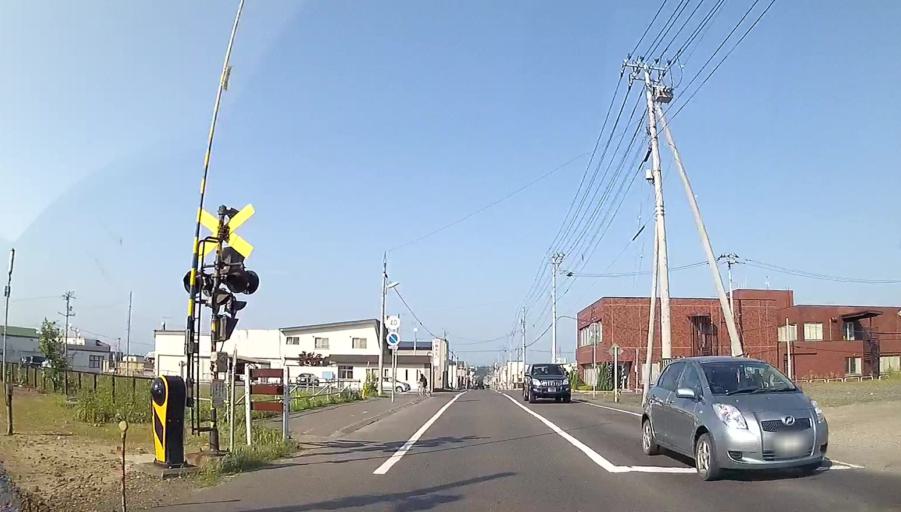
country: JP
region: Hokkaido
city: Otofuke
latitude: 43.0118
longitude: 142.8801
